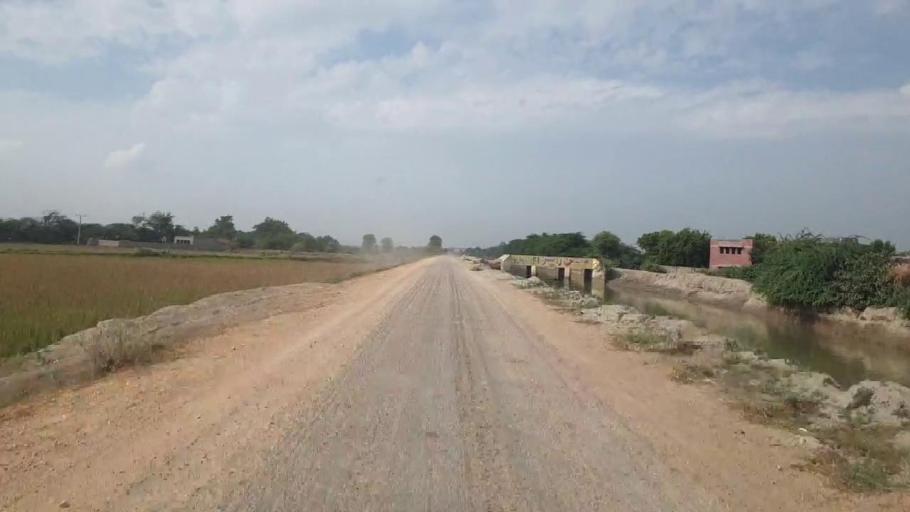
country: PK
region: Sindh
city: Kario
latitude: 24.6335
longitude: 68.5690
